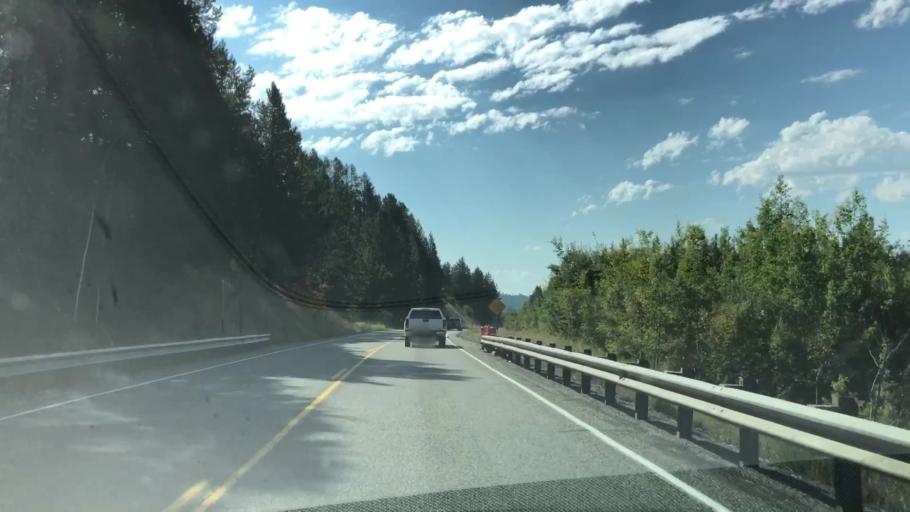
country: US
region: Idaho
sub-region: Teton County
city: Victor
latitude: 43.2890
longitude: -111.1223
